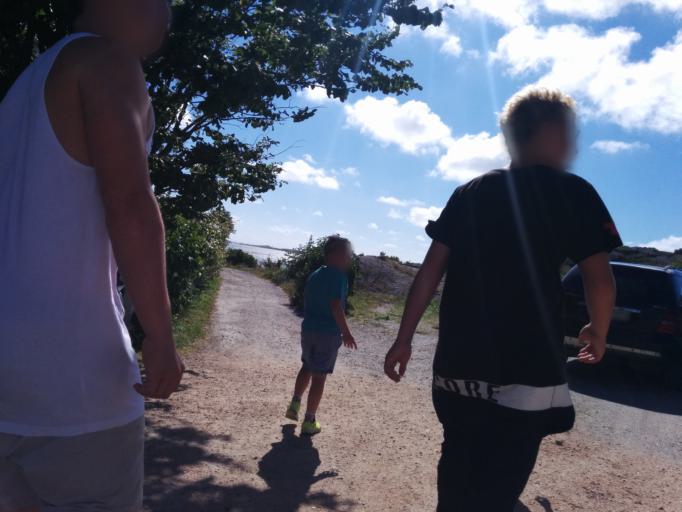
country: SE
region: Vaestra Goetaland
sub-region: Lysekils Kommun
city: Lysekil
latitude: 58.1238
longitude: 11.4396
